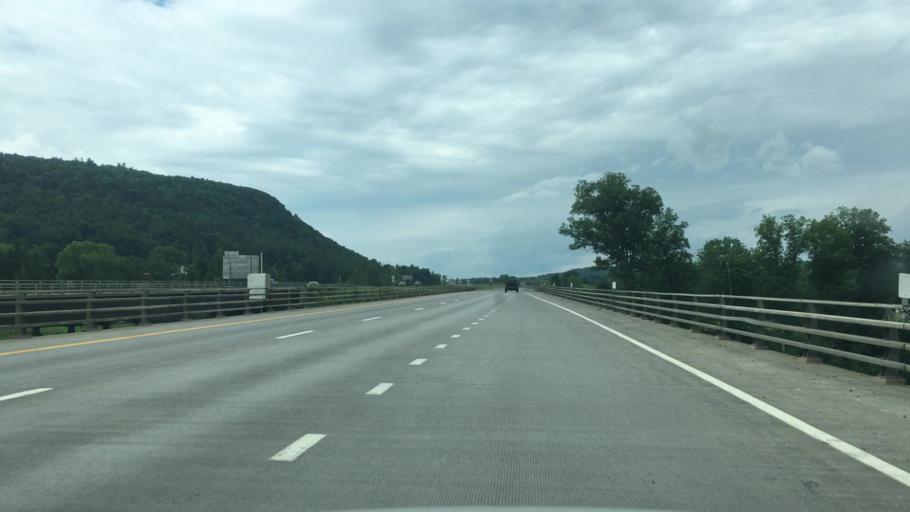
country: US
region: New York
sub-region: Schoharie County
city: Schoharie
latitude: 42.7059
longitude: -74.3219
